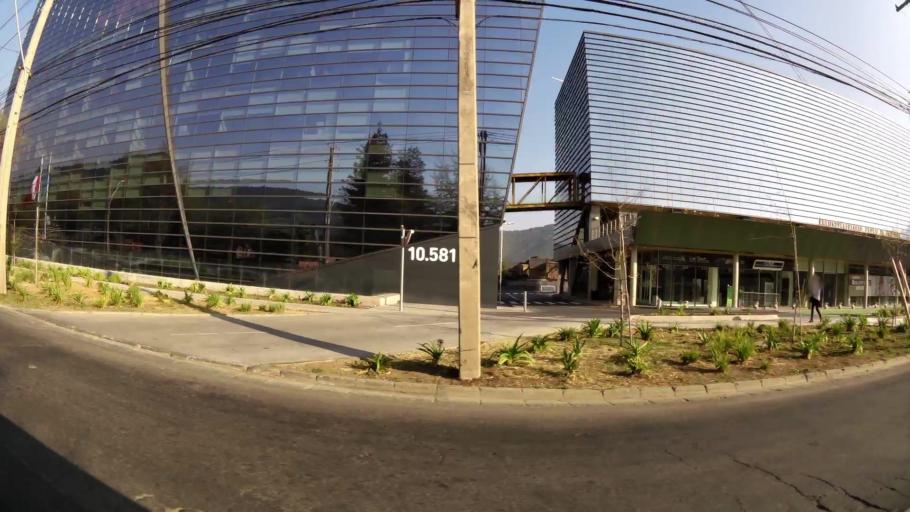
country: CL
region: Santiago Metropolitan
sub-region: Provincia de Santiago
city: Villa Presidente Frei, Nunoa, Santiago, Chile
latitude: -33.3554
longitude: -70.5354
